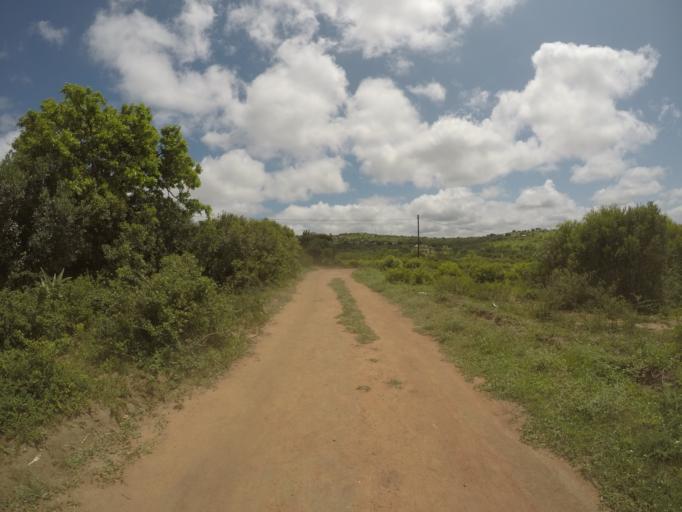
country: ZA
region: KwaZulu-Natal
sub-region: uThungulu District Municipality
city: Empangeni
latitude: -28.5823
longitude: 31.8368
